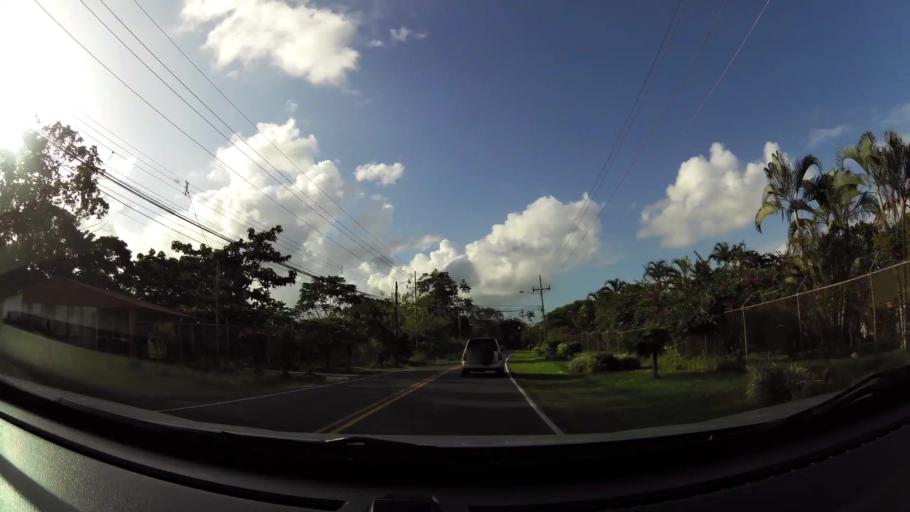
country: CR
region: Limon
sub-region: Canton de Siquirres
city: Siquirres
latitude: 10.0948
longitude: -83.5178
